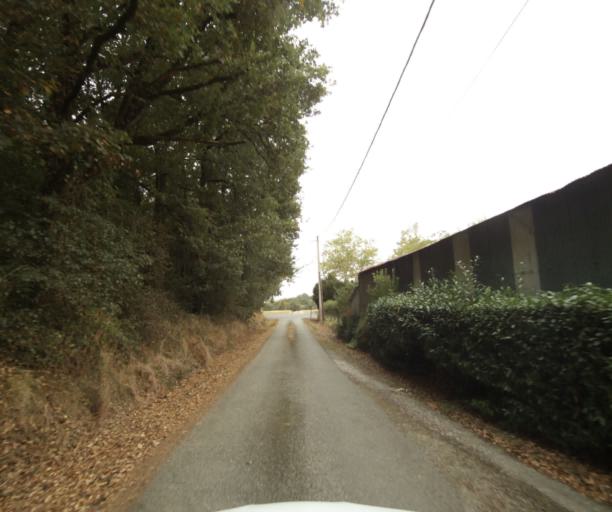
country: FR
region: Midi-Pyrenees
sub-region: Departement de la Haute-Garonne
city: Villefranche-de-Lauragais
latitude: 43.4156
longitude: 1.7423
